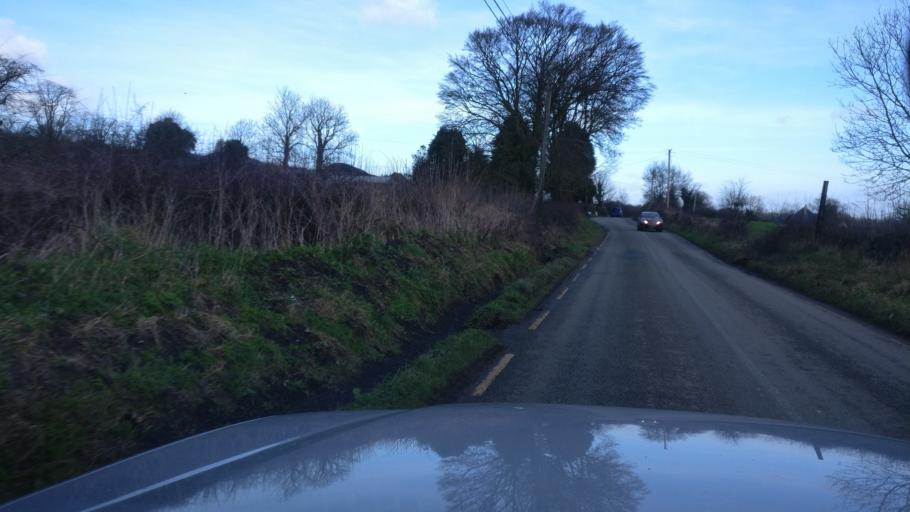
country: IE
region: Leinster
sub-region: Kilkenny
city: Castlecomer
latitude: 52.8308
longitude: -7.2001
